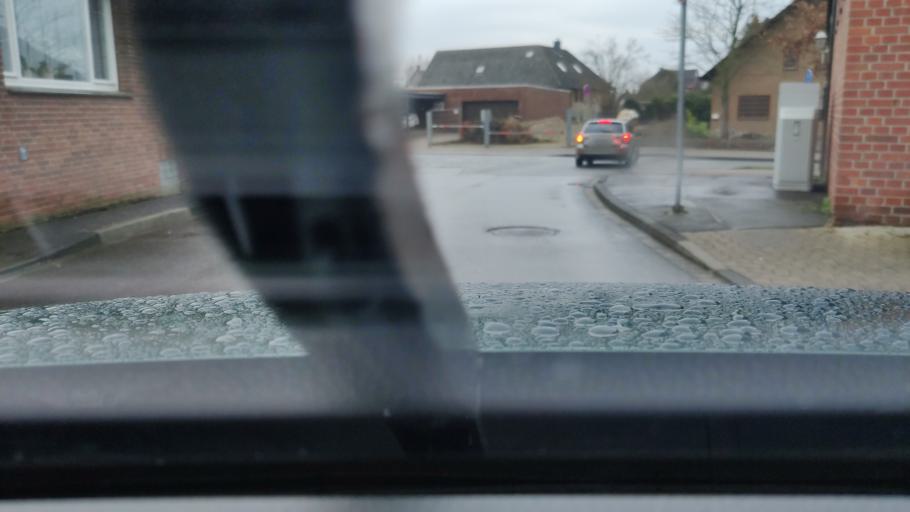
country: DE
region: Lower Saxony
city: Ilsede
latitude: 52.2667
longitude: 10.2225
